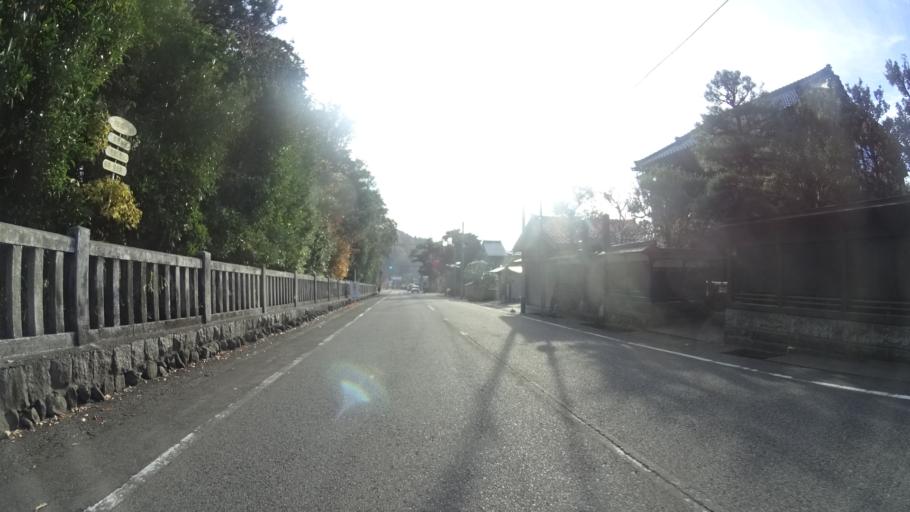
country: JP
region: Niigata
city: Yoshida-kasugacho
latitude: 37.7046
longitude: 138.8279
